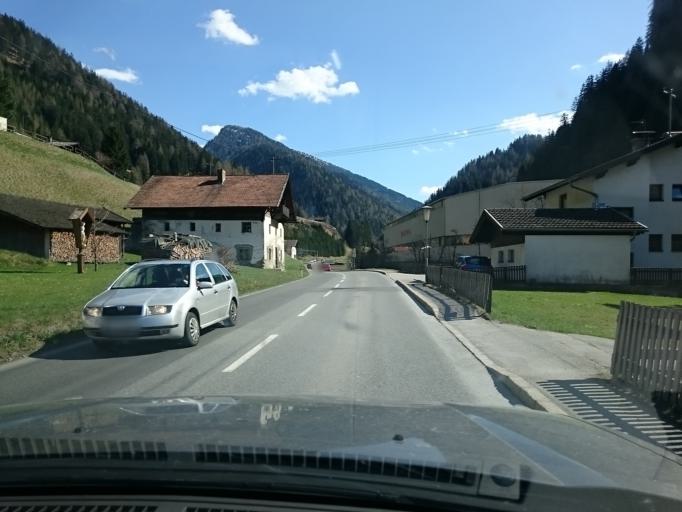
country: AT
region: Tyrol
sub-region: Politischer Bezirk Innsbruck Land
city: Steinach am Brenner
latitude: 47.0724
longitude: 11.4845
